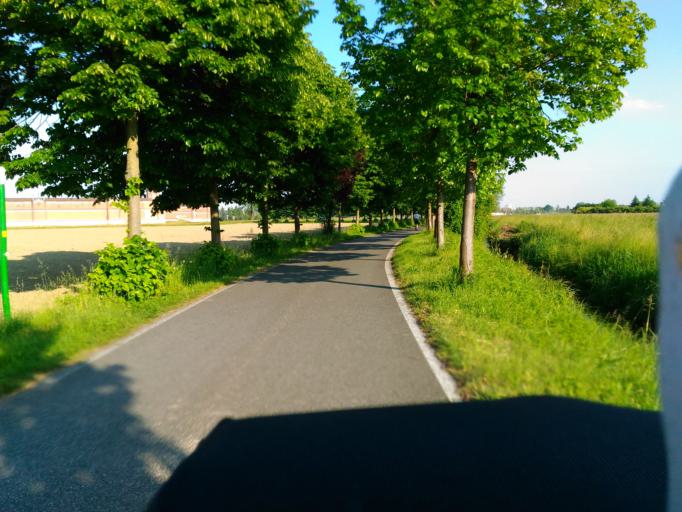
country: IT
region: Lombardy
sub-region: Provincia di Lodi
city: Montanaso Lombardo
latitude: 45.3218
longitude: 9.4688
